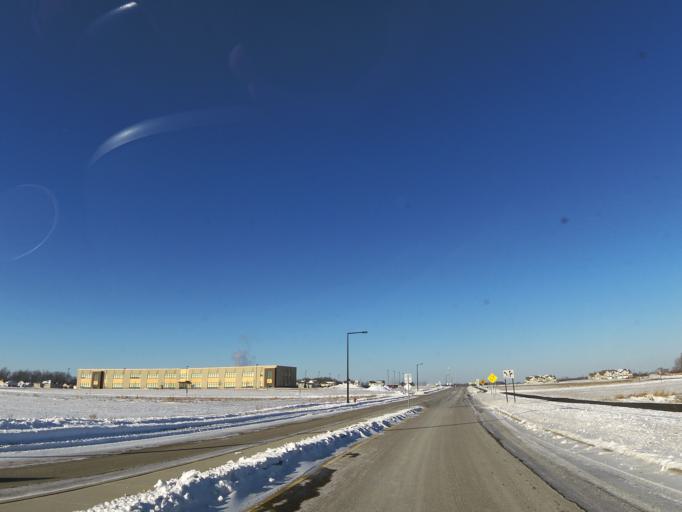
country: US
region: Minnesota
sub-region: Le Sueur County
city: New Prague
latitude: 44.5440
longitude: -93.5972
